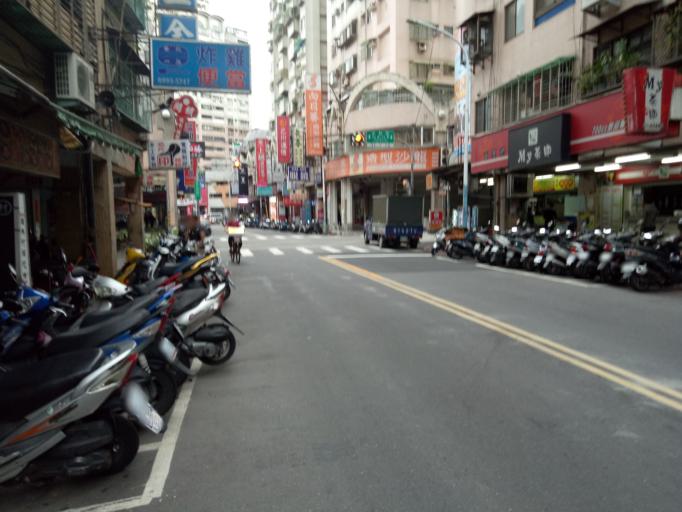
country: TW
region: Taipei
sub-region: Taipei
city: Banqiao
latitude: 25.0507
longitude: 121.4477
